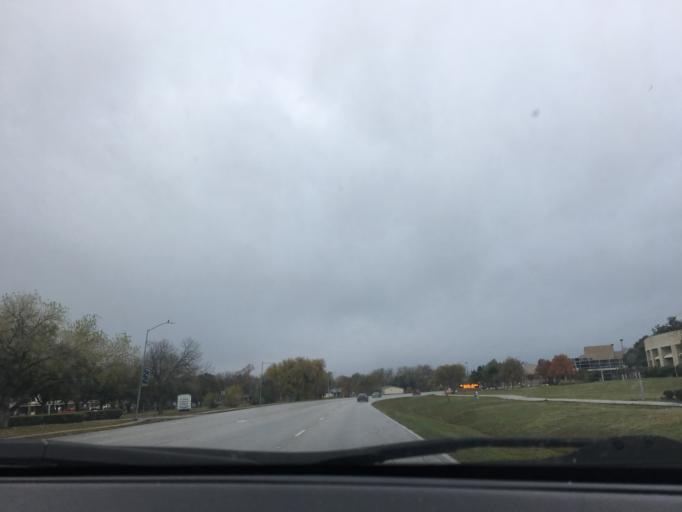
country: US
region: Texas
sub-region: Hays County
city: San Marcos
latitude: 29.8854
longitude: -97.9304
